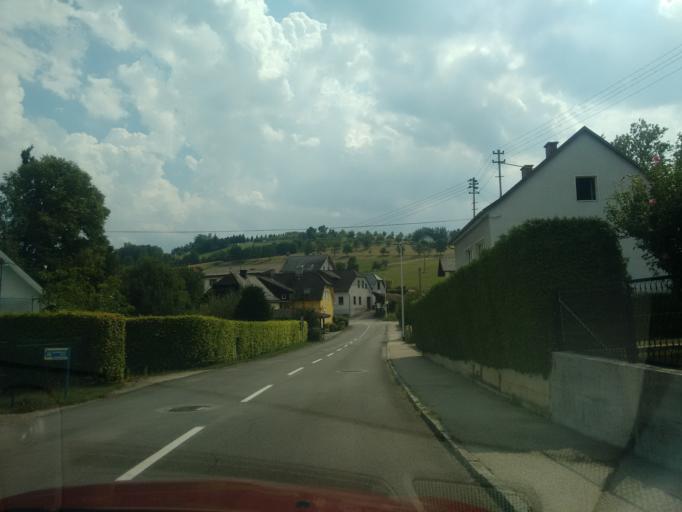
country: AT
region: Upper Austria
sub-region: Politischer Bezirk Grieskirchen
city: Bad Schallerbach
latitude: 48.2401
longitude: 13.9122
